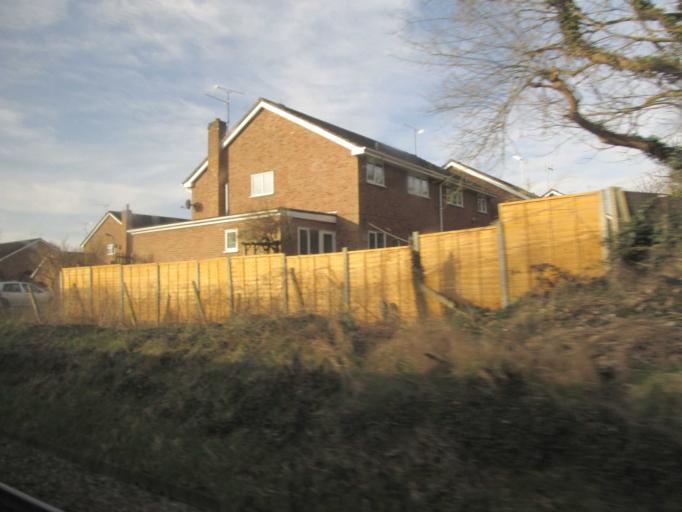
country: GB
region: England
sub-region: Hampshire
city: Farnborough
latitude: 51.2955
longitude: -0.7405
